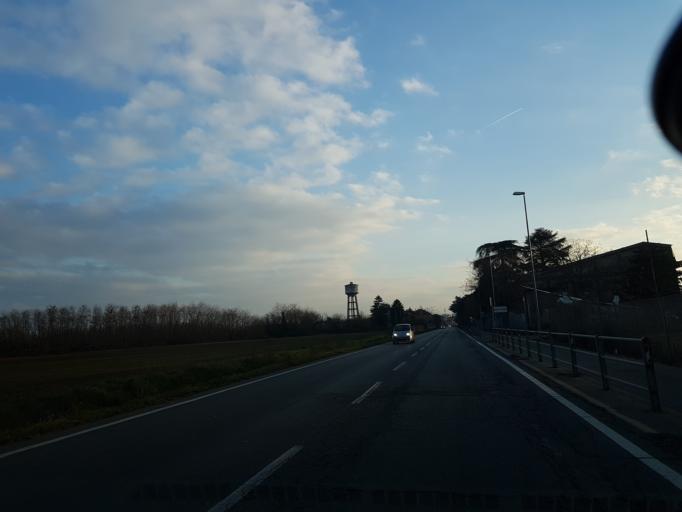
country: IT
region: Piedmont
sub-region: Provincia di Alessandria
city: Novi Ligure
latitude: 44.7793
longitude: 8.7893
